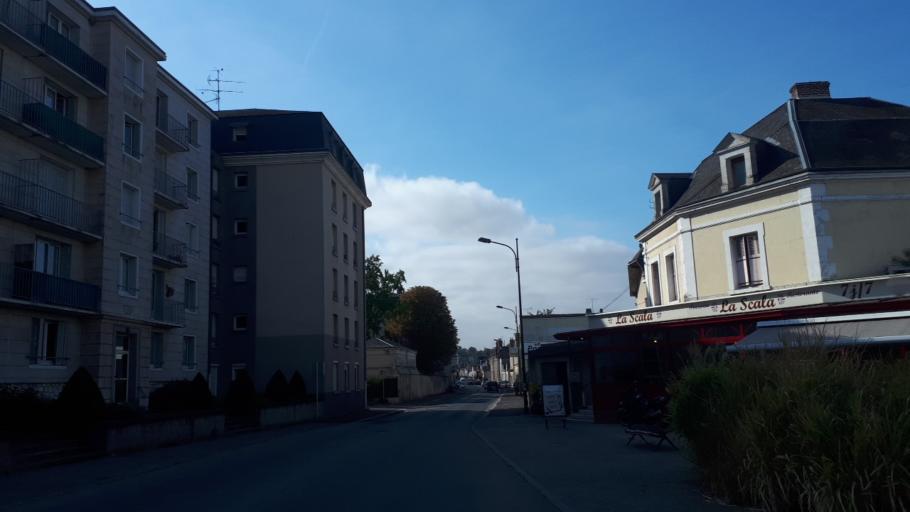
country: FR
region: Centre
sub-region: Departement du Loir-et-Cher
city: Vendome
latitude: 47.8017
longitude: 1.0699
